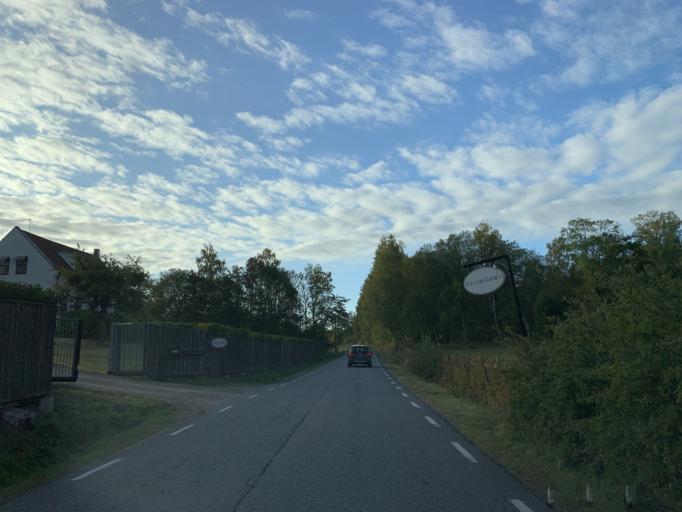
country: SE
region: Stockholm
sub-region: Upplands-Bro Kommun
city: Bro
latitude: 59.5054
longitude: 17.5854
